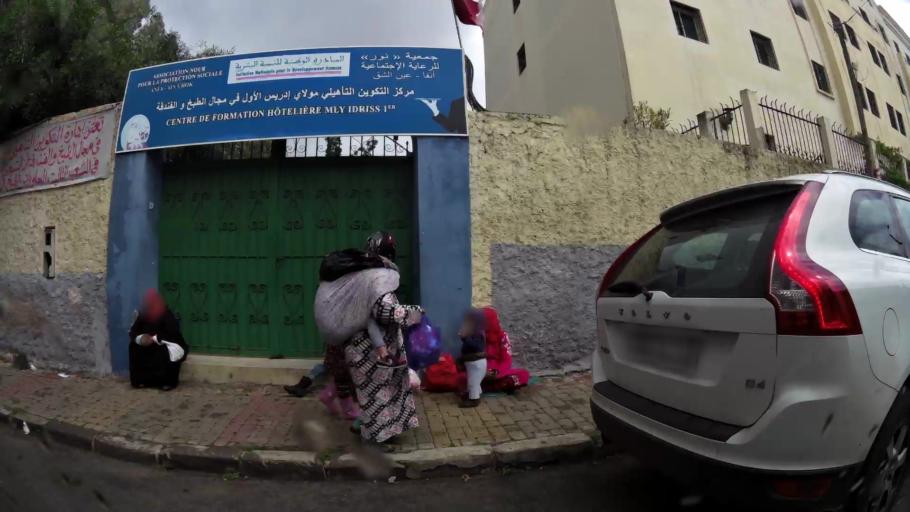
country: MA
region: Grand Casablanca
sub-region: Casablanca
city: Casablanca
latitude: 33.5718
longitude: -7.6170
